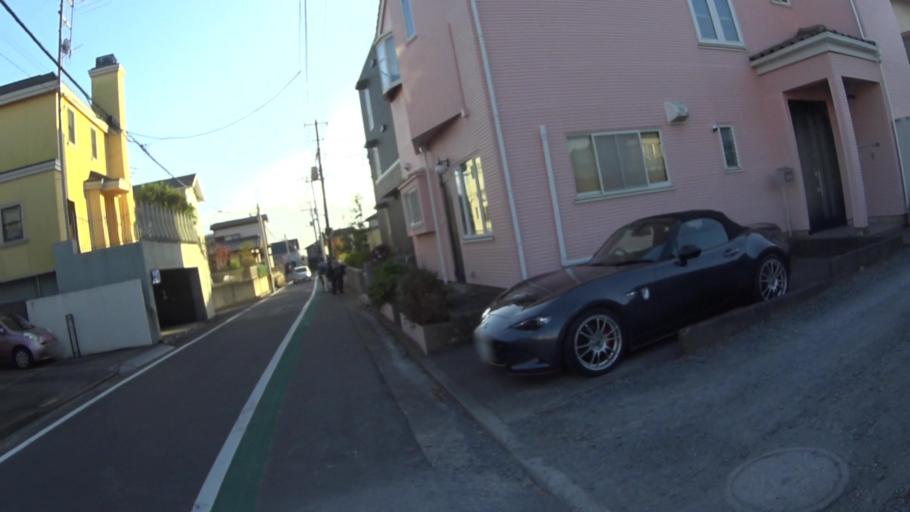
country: JP
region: Ibaraki
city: Mito-shi
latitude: 36.3747
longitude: 140.4624
